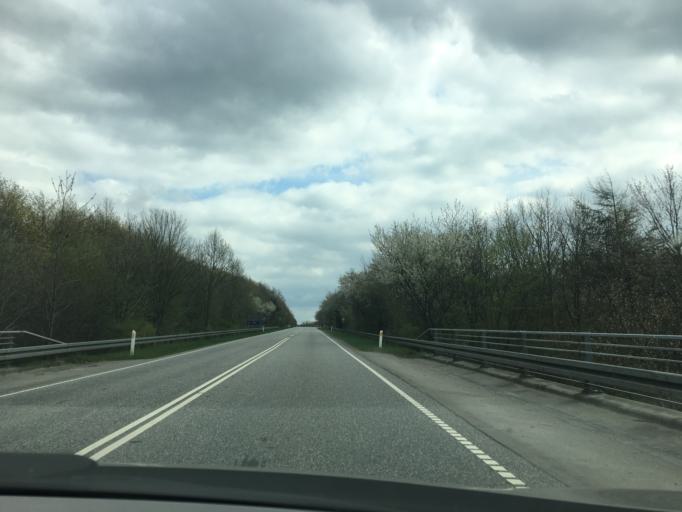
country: DK
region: Central Jutland
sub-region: Horsens Kommune
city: Braedstrup
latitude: 55.9655
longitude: 9.6055
